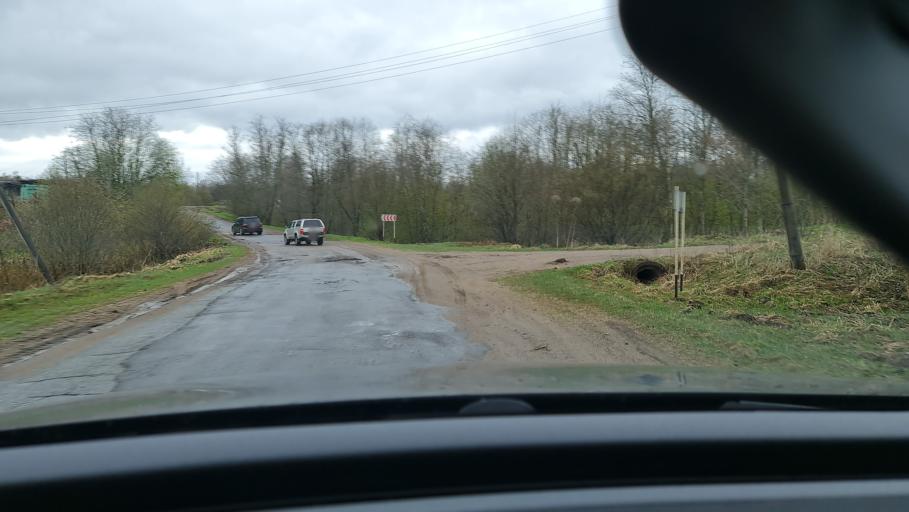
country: RU
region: Novgorod
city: Marevo
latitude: 57.2407
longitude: 32.0431
